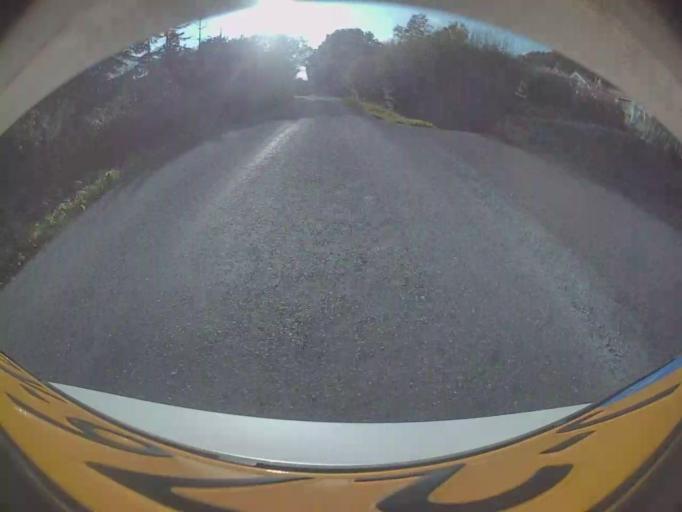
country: IE
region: Leinster
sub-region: Wicklow
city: Enniskerry
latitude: 53.1891
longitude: -6.2355
